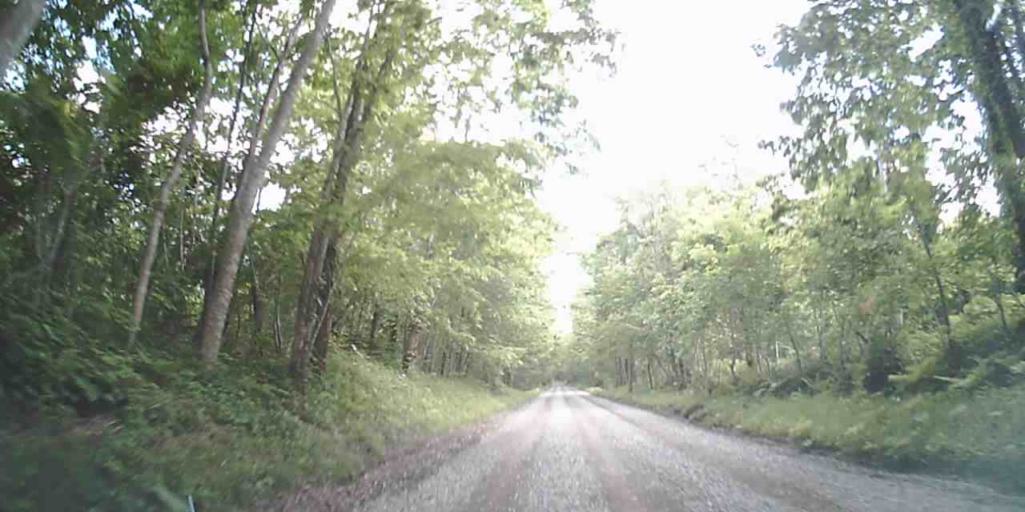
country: JP
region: Hokkaido
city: Tomakomai
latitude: 42.7587
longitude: 141.4270
